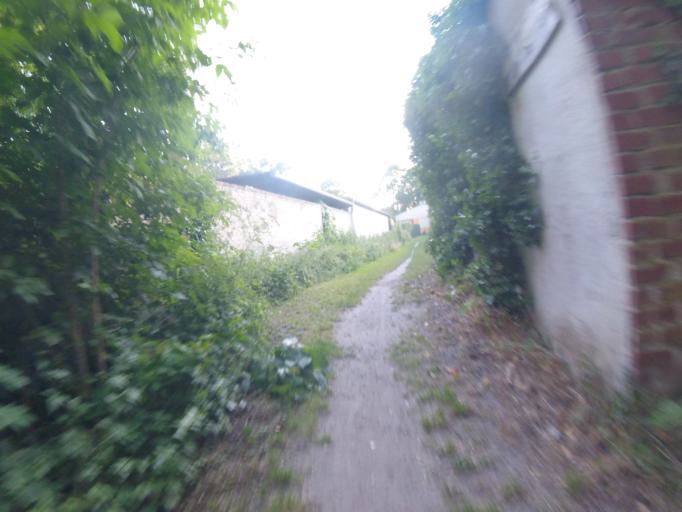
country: DE
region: Brandenburg
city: Mittenwalde
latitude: 52.2677
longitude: 13.5406
